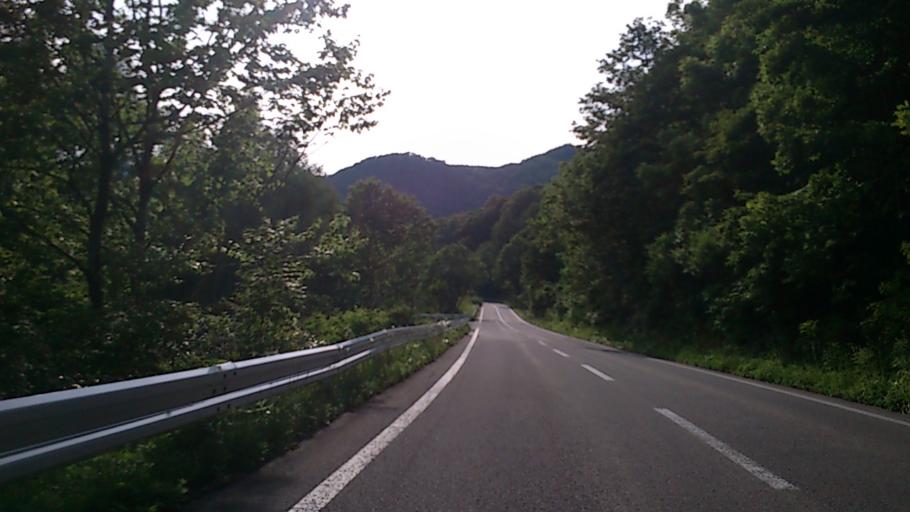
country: JP
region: Aomori
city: Aomori Shi
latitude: 40.6509
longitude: 140.7724
